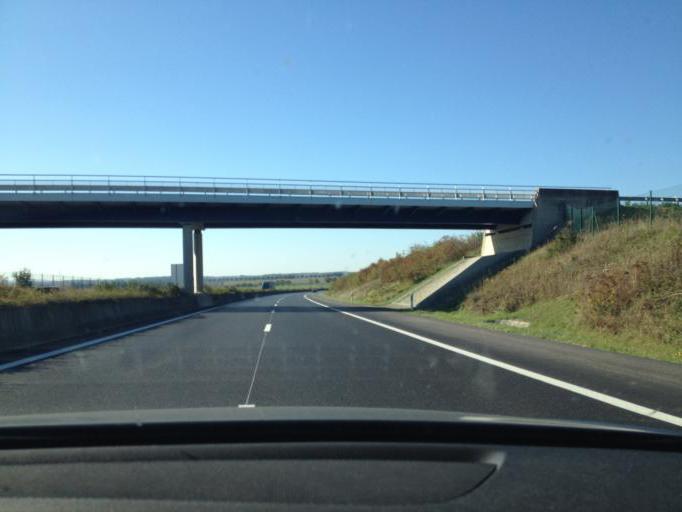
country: LU
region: Grevenmacher
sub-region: Canton de Remich
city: Mondorf-les-Bains
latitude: 49.4946
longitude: 6.3184
